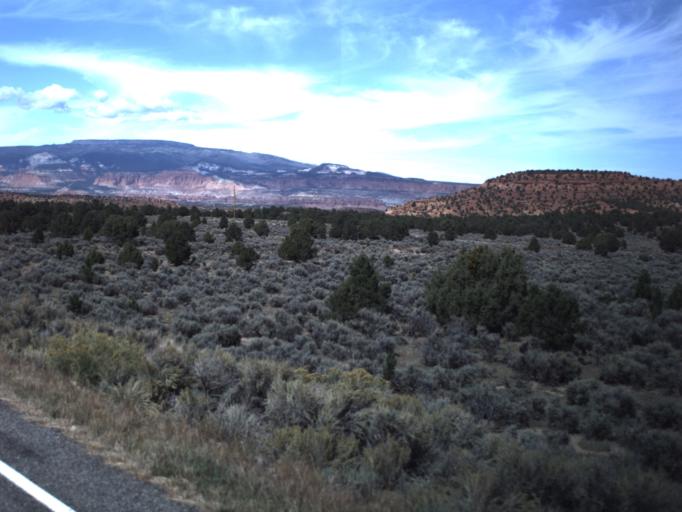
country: US
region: Utah
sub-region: Wayne County
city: Loa
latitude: 38.2373
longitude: -111.3724
